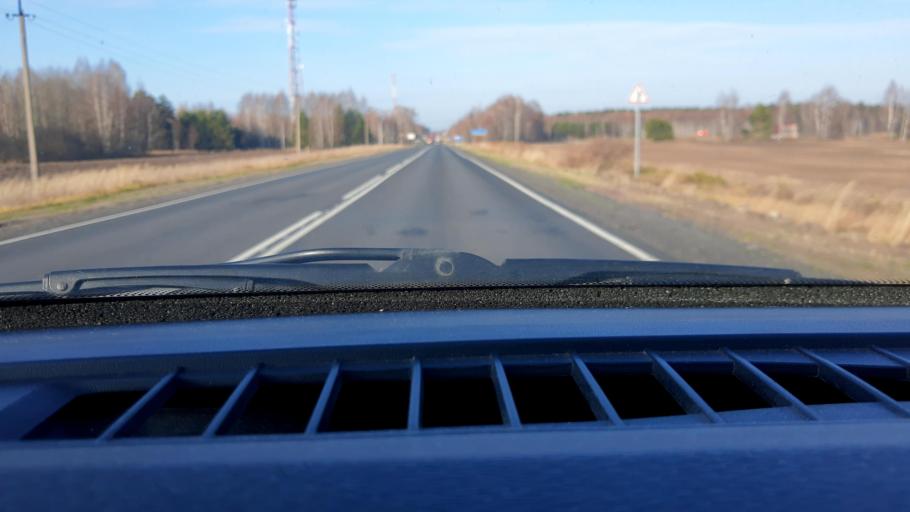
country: RU
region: Nizjnij Novgorod
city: Novaya Balakhna
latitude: 56.5955
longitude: 43.6470
